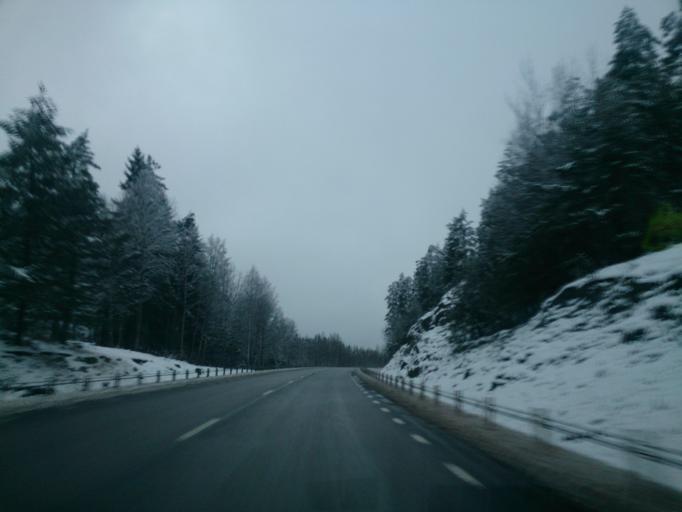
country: SE
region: OEstergoetland
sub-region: Atvidabergs Kommun
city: Atvidaberg
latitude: 58.2389
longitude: 15.9397
